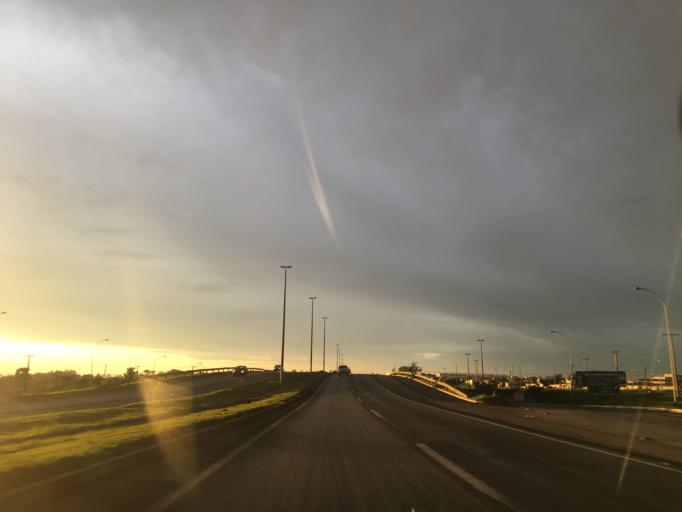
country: BR
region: Federal District
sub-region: Brasilia
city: Brasilia
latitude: -16.0006
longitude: -47.9847
